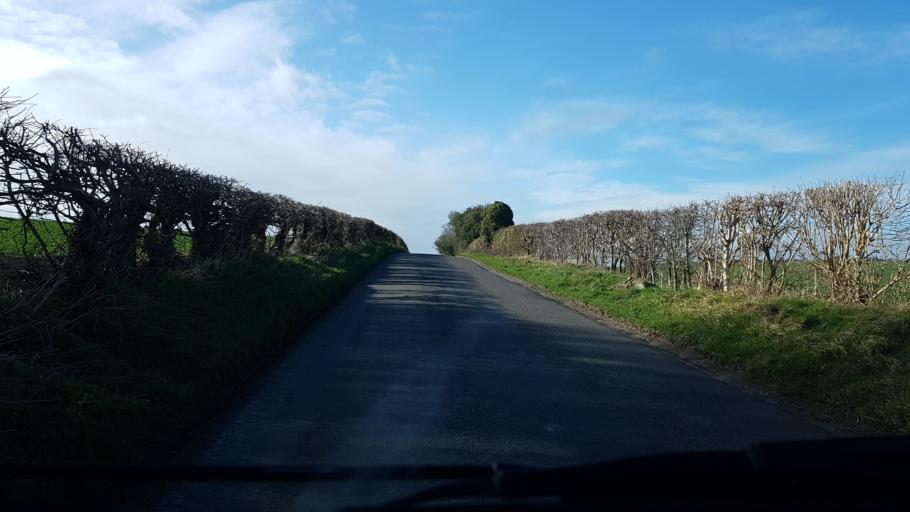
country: GB
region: England
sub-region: Wiltshire
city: Huish
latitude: 51.3971
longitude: -1.8145
